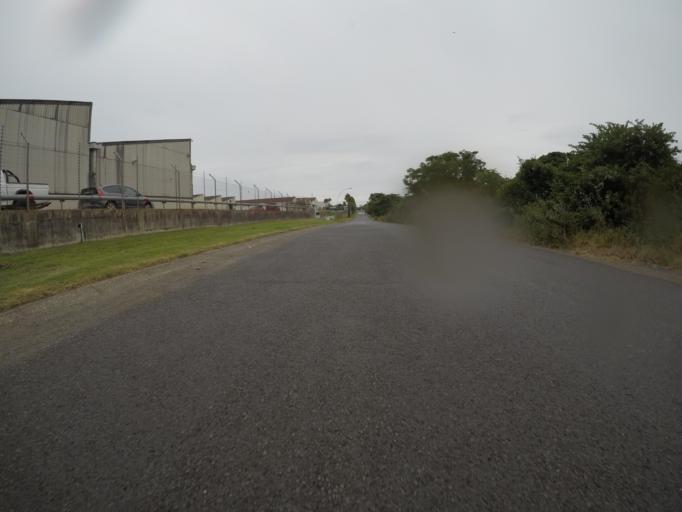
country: ZA
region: Eastern Cape
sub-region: Buffalo City Metropolitan Municipality
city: East London
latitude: -32.9696
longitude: 27.8191
